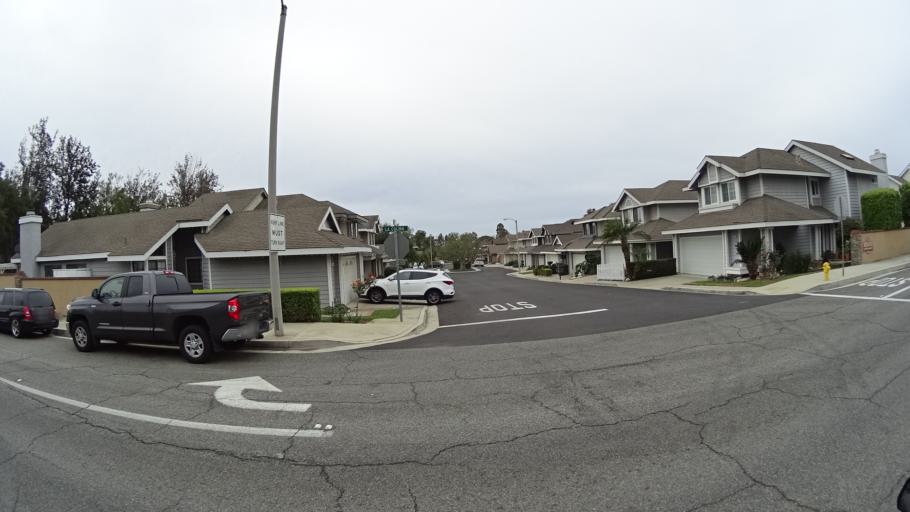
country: US
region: California
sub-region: Orange County
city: North Tustin
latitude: 33.7528
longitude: -117.8023
